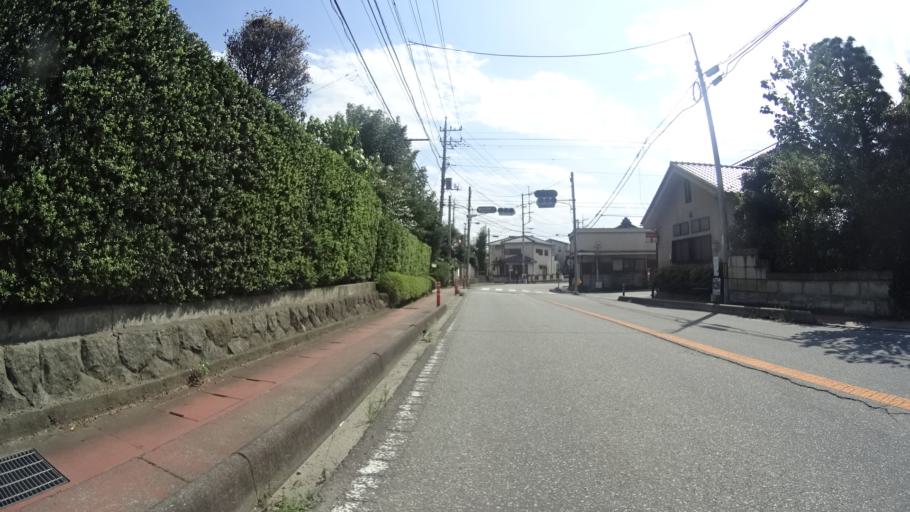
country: JP
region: Yamanashi
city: Enzan
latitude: 35.7114
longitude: 138.7331
